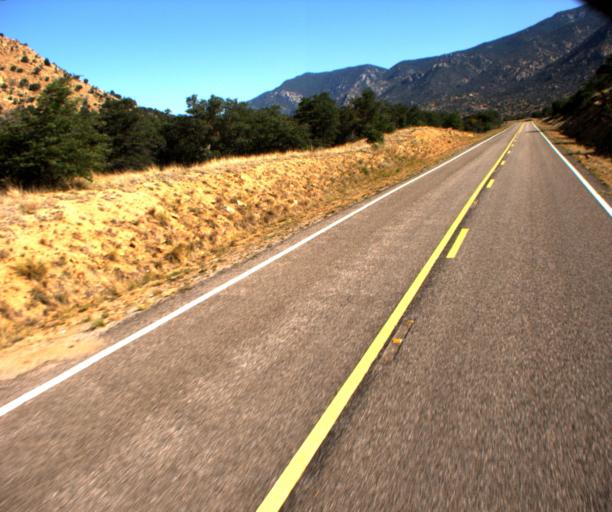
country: US
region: Arizona
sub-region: Graham County
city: Swift Trail Junction
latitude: 32.5868
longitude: -109.8543
